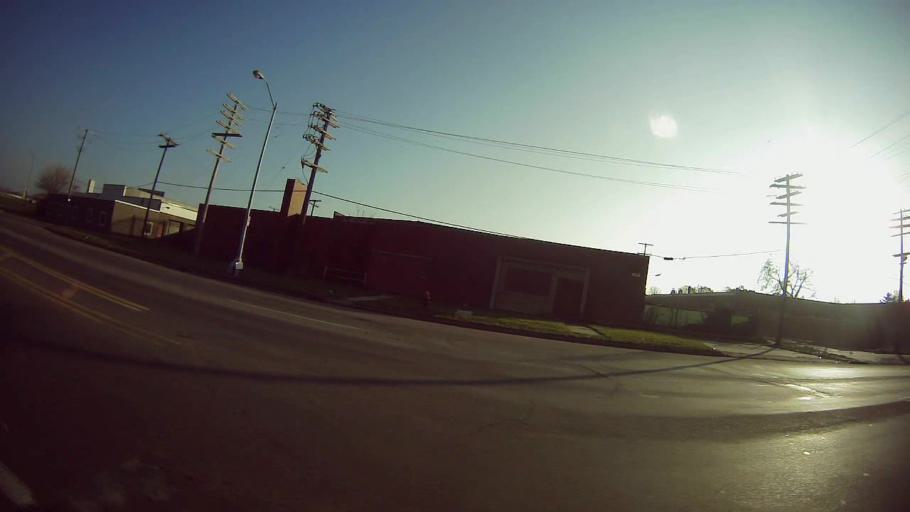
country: US
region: Michigan
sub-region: Wayne County
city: Dearborn
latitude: 42.3725
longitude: -83.1975
